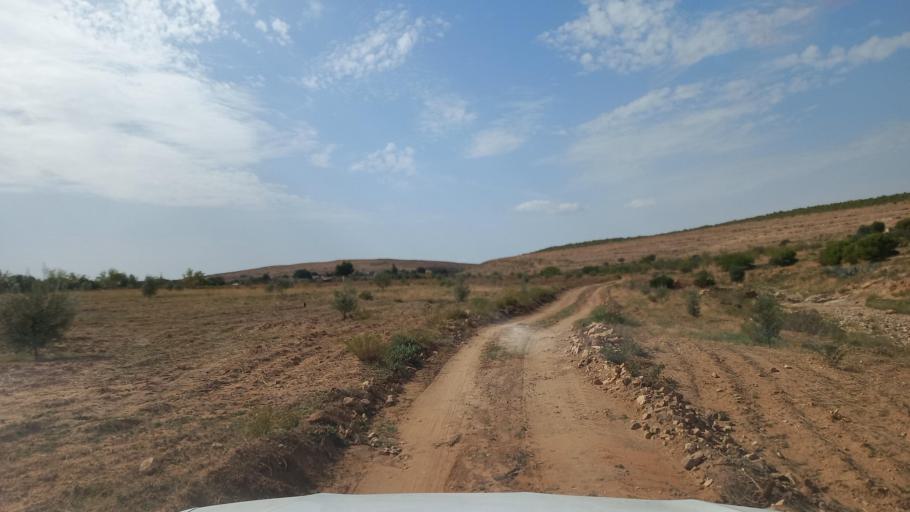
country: TN
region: Al Qasrayn
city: Kasserine
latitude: 35.3639
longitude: 8.8584
